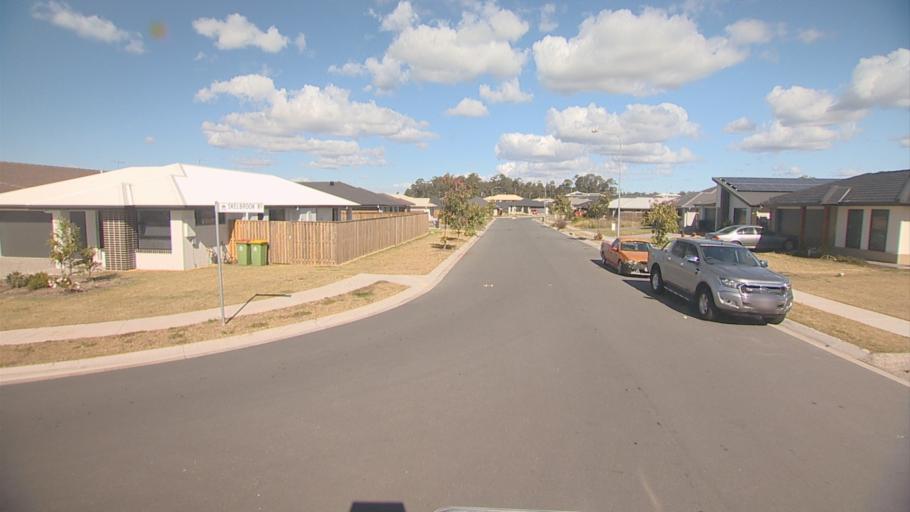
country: AU
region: Queensland
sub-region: Logan
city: Logan Reserve
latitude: -27.7128
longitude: 153.0847
